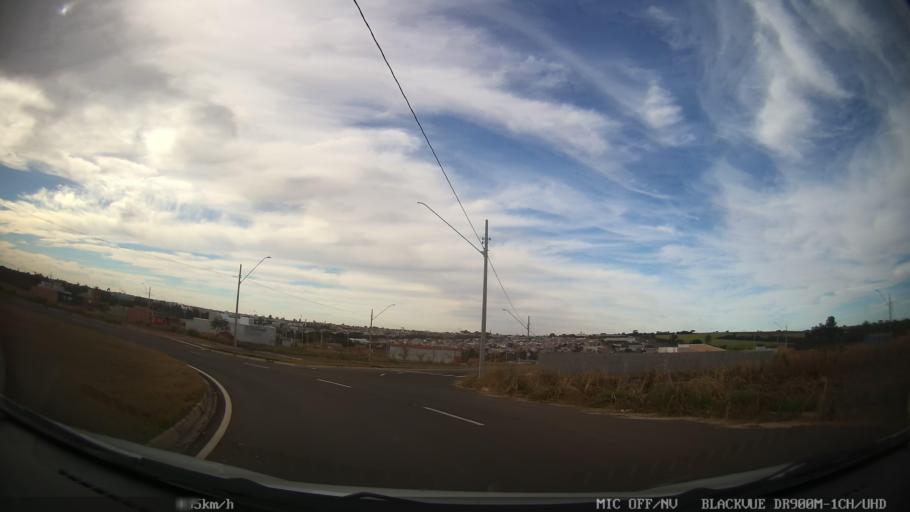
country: BR
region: Sao Paulo
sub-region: Catanduva
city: Catanduva
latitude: -21.1392
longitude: -49.0098
